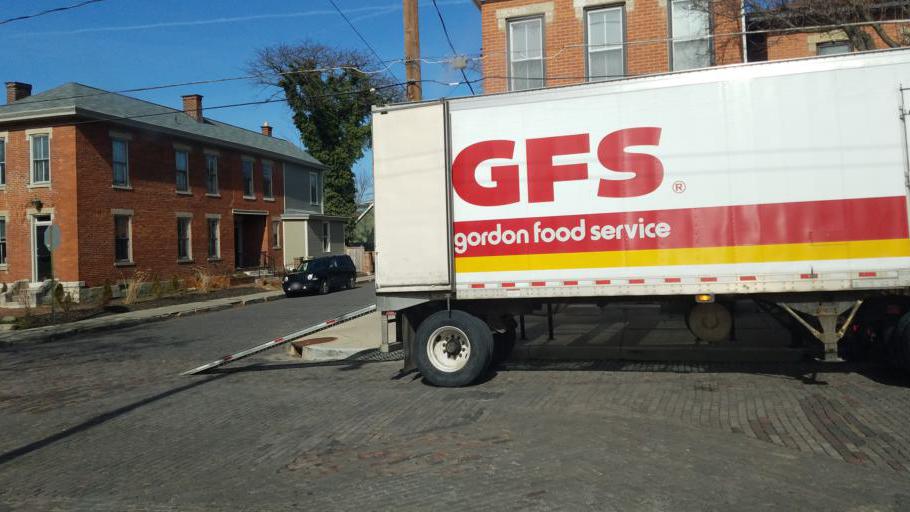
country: US
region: Ohio
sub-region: Franklin County
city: Columbus
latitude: 39.9489
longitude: -82.9909
